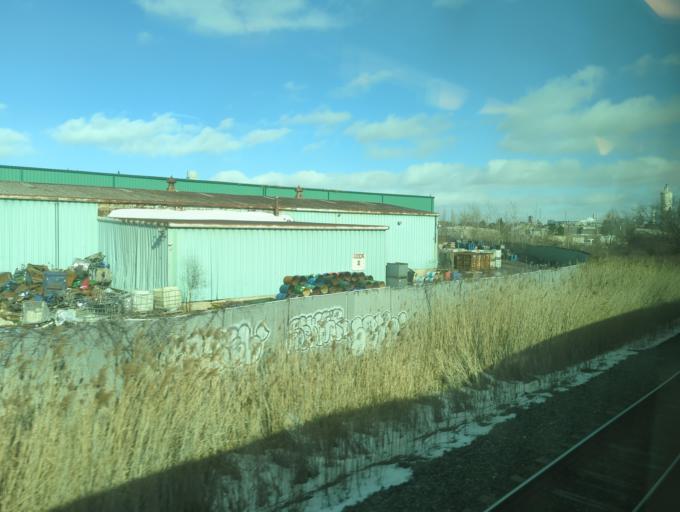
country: CA
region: Ontario
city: Burlington
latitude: 43.3733
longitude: -79.7676
